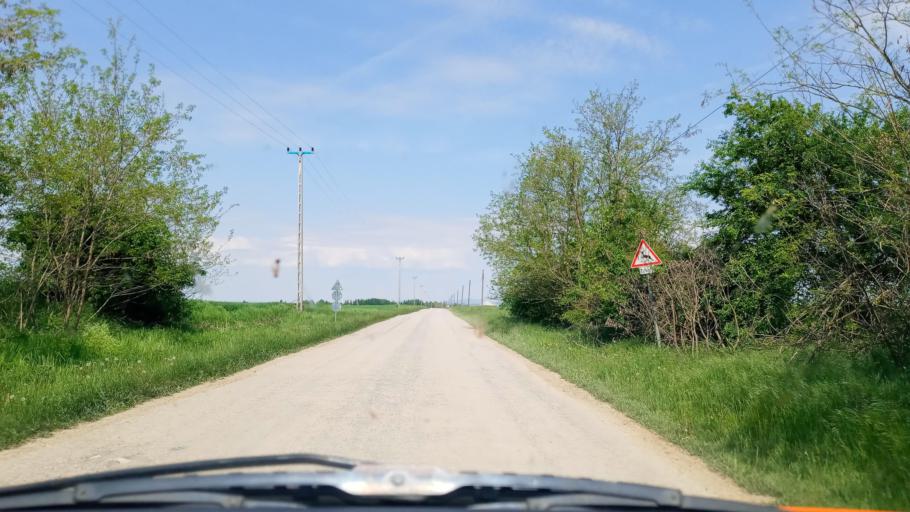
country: HU
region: Baranya
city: Boly
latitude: 45.8980
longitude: 18.5566
